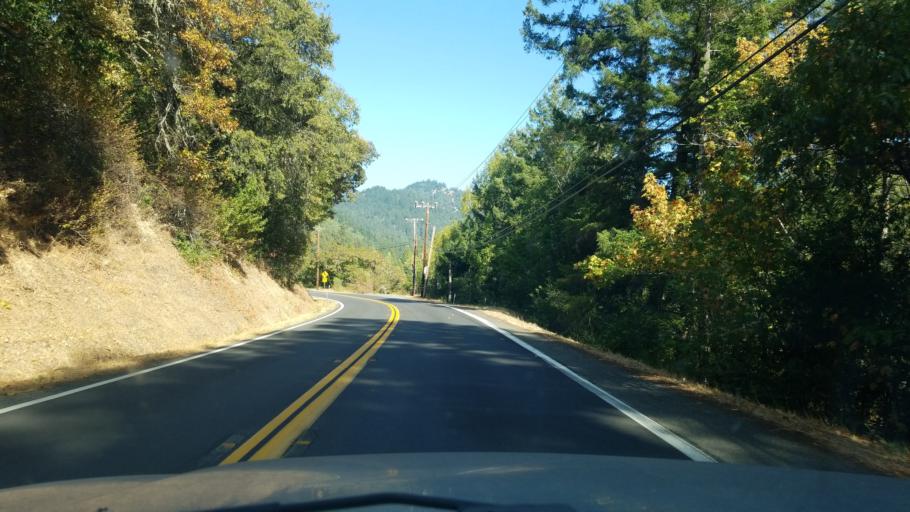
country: US
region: California
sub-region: Humboldt County
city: Redway
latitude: 40.2193
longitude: -123.8105
